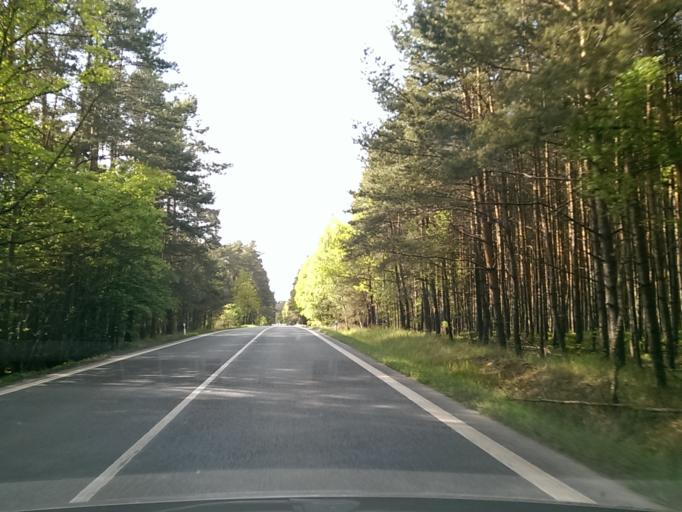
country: CZ
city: Doksy
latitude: 50.5363
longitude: 14.6842
